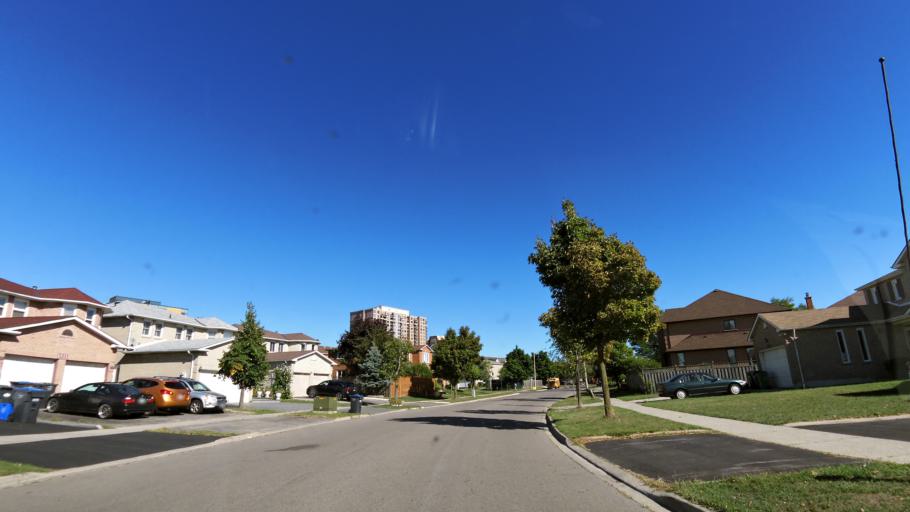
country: CA
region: Ontario
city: Mississauga
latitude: 43.6107
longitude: -79.6638
